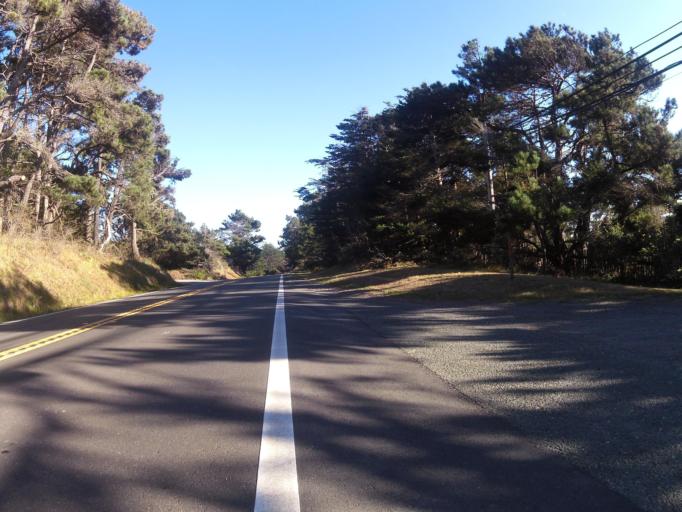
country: US
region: California
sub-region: Sonoma County
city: Sea Ranch
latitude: 38.7953
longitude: -123.5674
